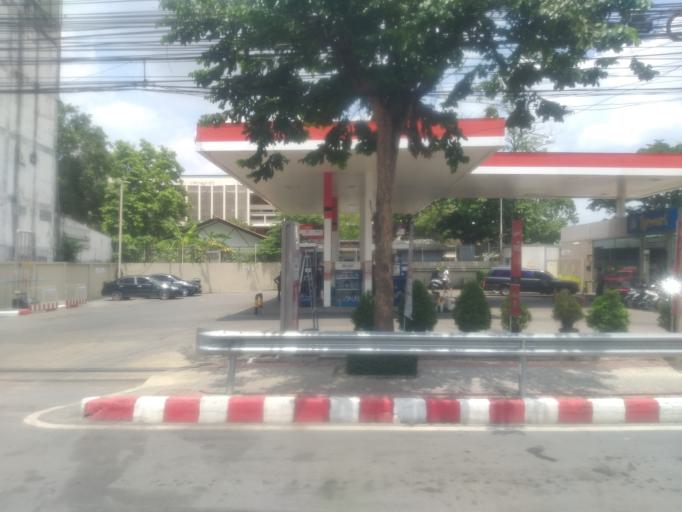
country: TH
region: Bangkok
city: Din Daeng
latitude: 13.7755
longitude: 100.5549
